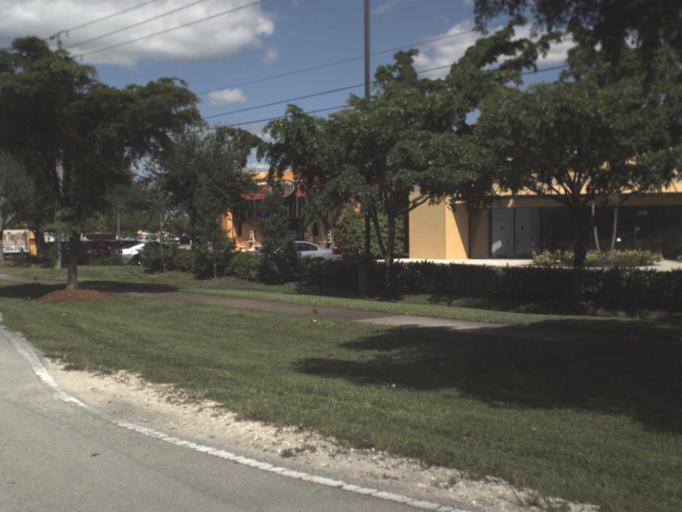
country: US
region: Florida
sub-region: Collier County
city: Lely
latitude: 26.1193
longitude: -81.7587
